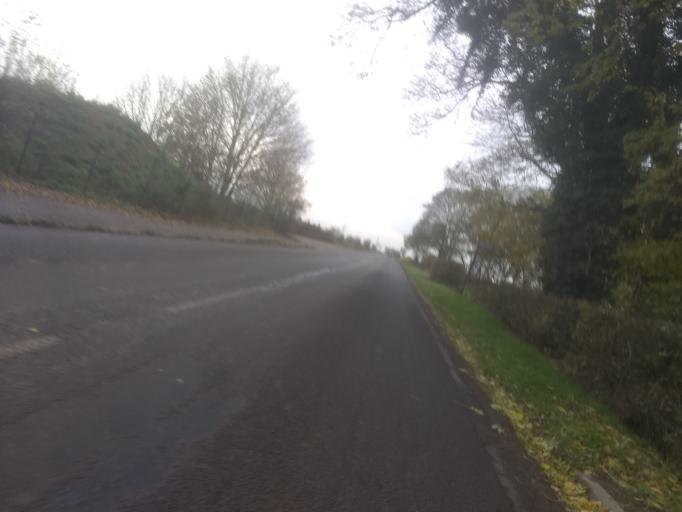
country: FR
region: Nord-Pas-de-Calais
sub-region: Departement du Pas-de-Calais
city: Dainville
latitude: 50.2792
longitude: 2.7374
